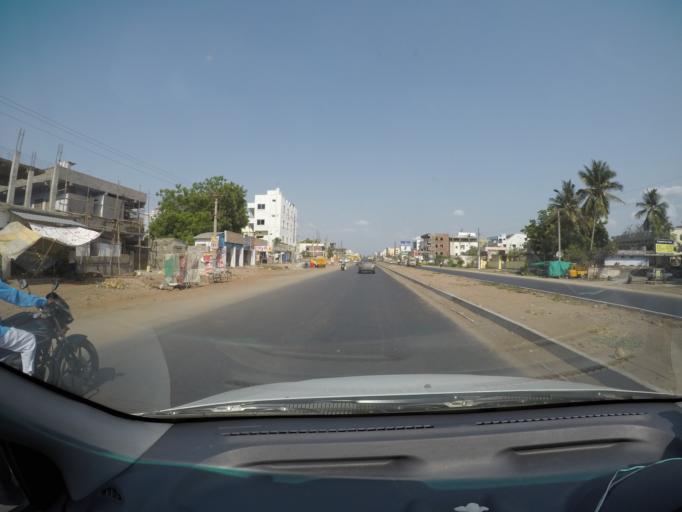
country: IN
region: Andhra Pradesh
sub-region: Krishna
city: Yanamalakuduru
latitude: 16.4790
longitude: 80.6997
